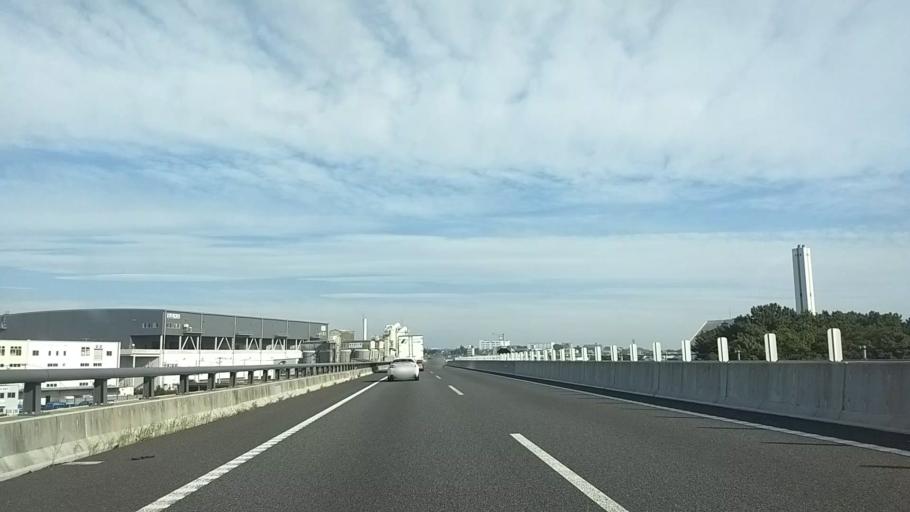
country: JP
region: Kanagawa
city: Atsugi
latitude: 35.4545
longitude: 139.3735
